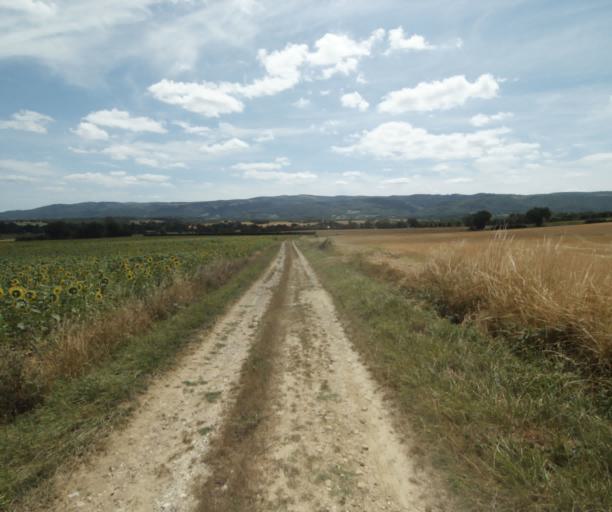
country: FR
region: Midi-Pyrenees
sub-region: Departement du Tarn
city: Soreze
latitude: 43.4902
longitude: 2.0719
